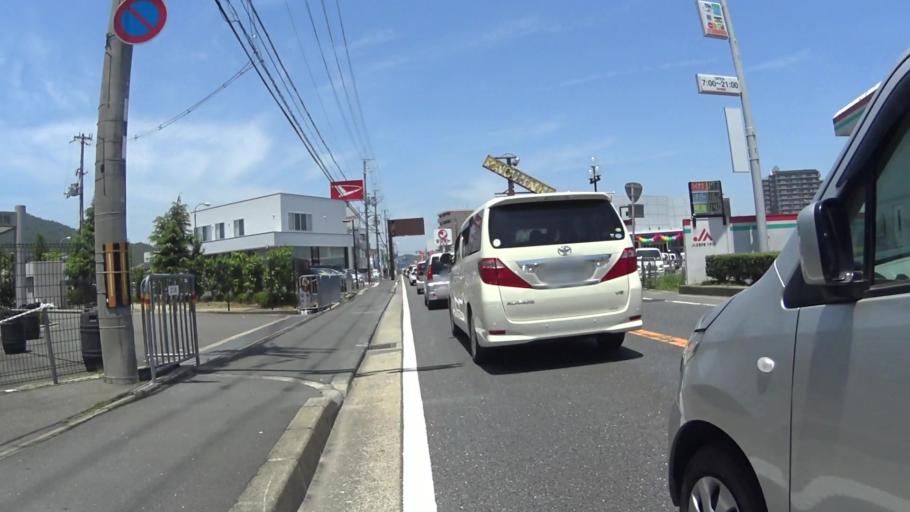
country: JP
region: Kyoto
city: Kameoka
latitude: 35.0316
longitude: 135.5526
